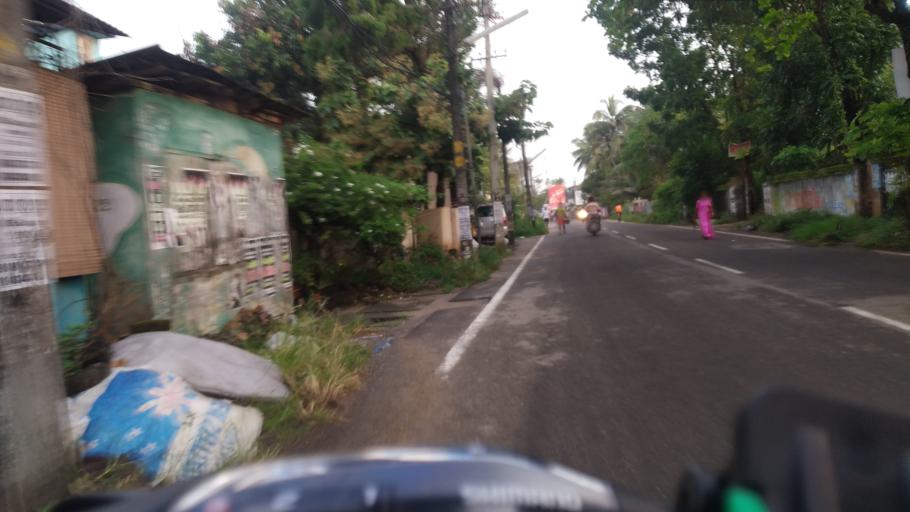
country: IN
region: Kerala
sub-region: Ernakulam
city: Cochin
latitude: 9.9800
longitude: 76.2410
